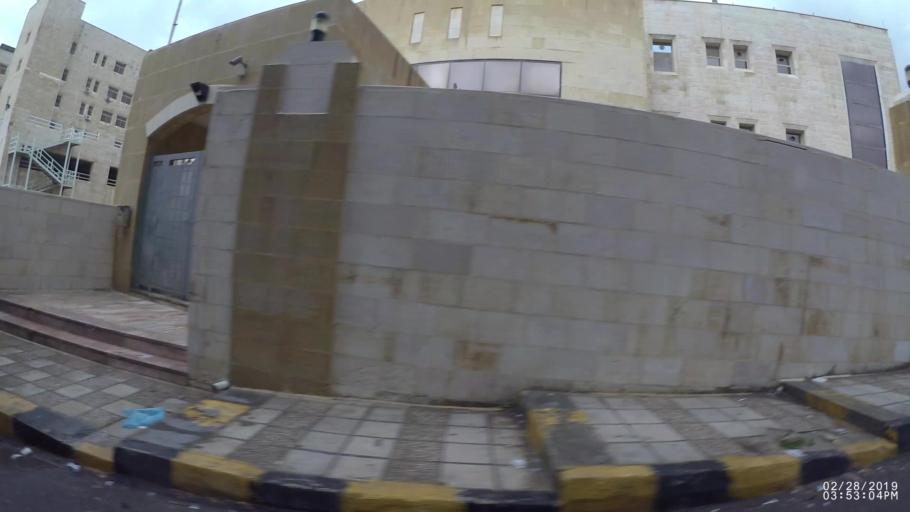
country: JO
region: Amman
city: Amman
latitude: 31.9951
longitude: 35.9266
